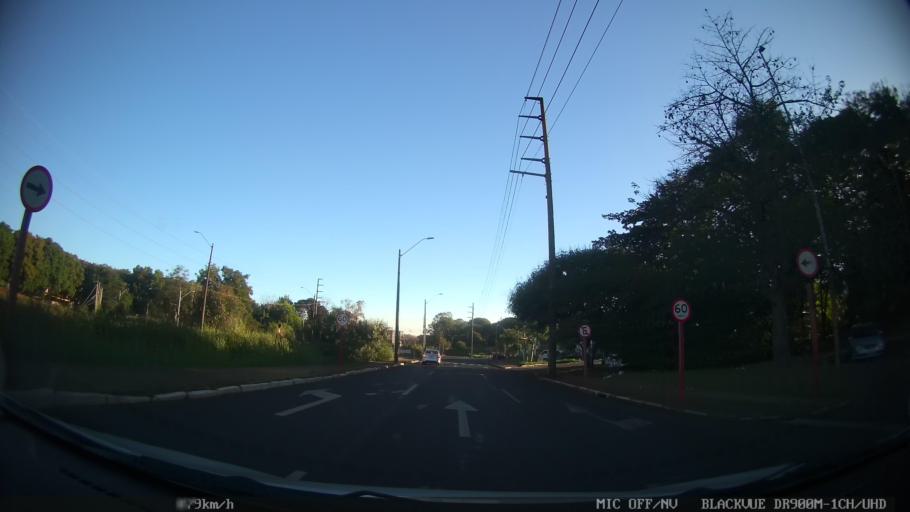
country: BR
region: Sao Paulo
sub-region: Araraquara
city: Araraquara
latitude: -21.8089
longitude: -48.1757
